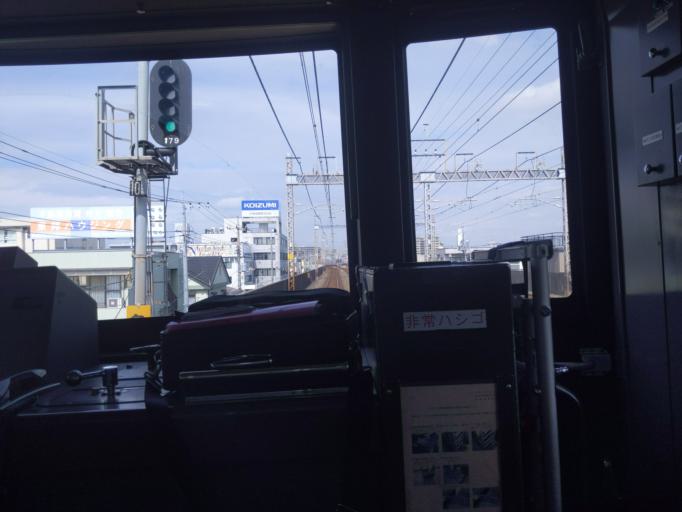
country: JP
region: Saitama
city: Soka
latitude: 35.8322
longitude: 139.8038
